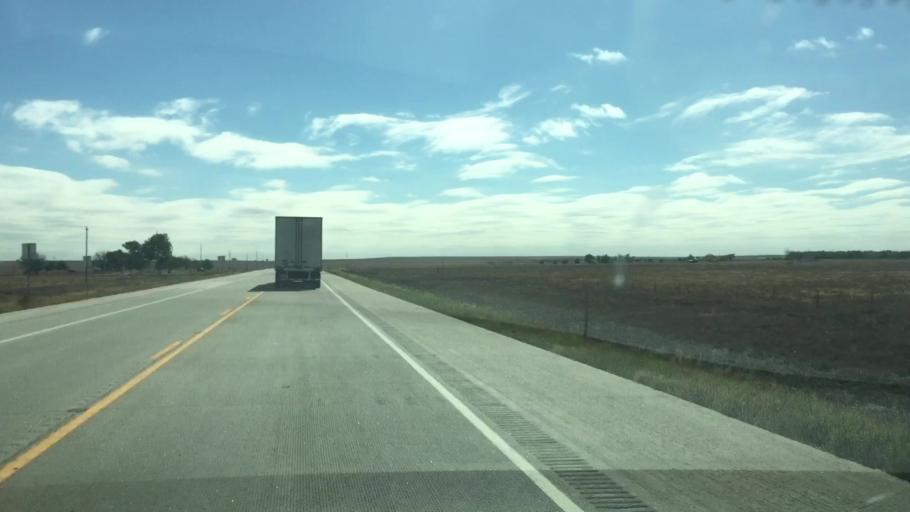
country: US
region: Colorado
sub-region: Lincoln County
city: Hugo
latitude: 39.0541
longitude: -103.3539
